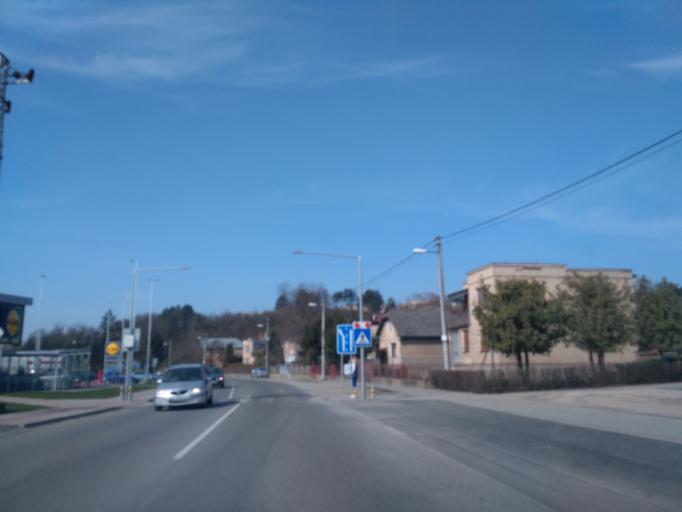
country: SK
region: Kosicky
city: Moldava nad Bodvou
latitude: 48.6099
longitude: 20.9952
